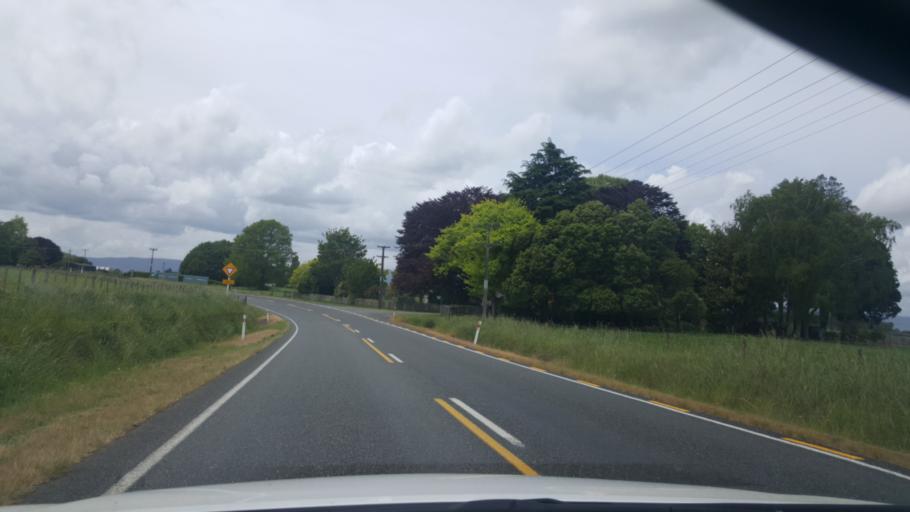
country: NZ
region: Waikato
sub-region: Matamata-Piako District
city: Matamata
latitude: -37.8756
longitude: 175.7225
